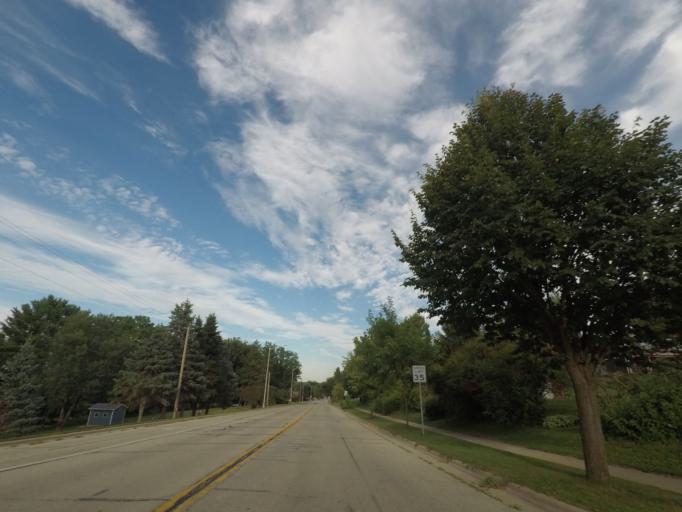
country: US
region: Wisconsin
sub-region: Green County
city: New Glarus
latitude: 42.8145
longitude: -89.6448
